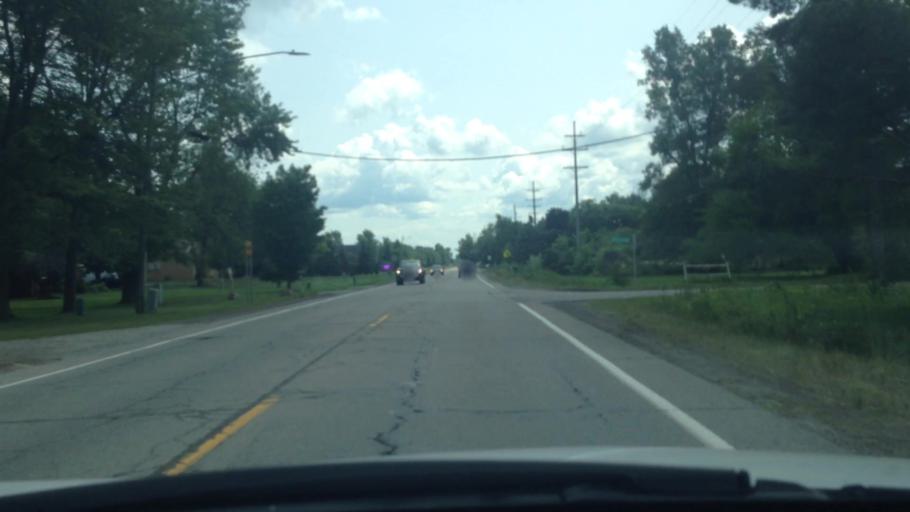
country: US
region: Michigan
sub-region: Wayne County
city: Flat Rock
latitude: 42.1599
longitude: -83.3056
